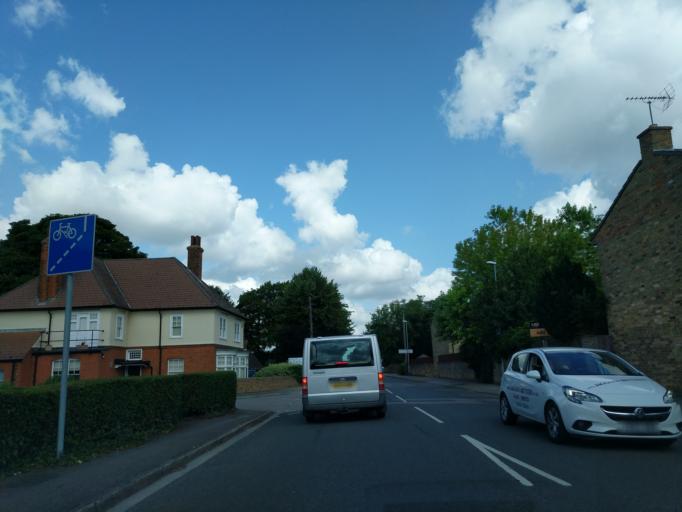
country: GB
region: England
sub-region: Suffolk
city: Exning
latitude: 52.3071
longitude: 0.3844
